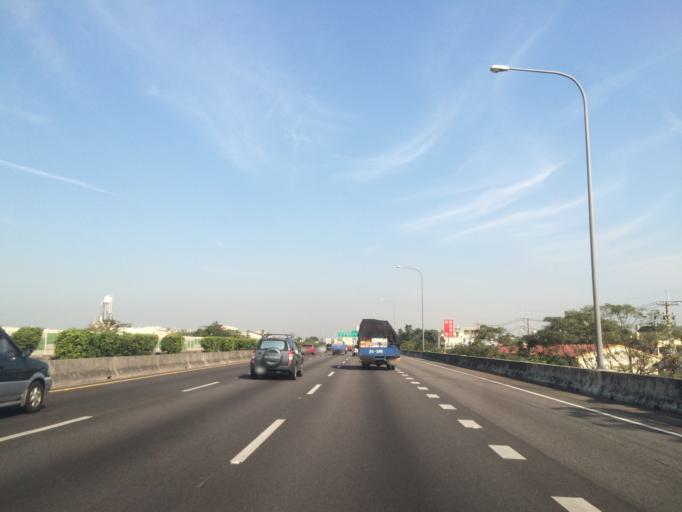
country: TW
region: Taiwan
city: Fengyuan
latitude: 24.2395
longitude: 120.6890
